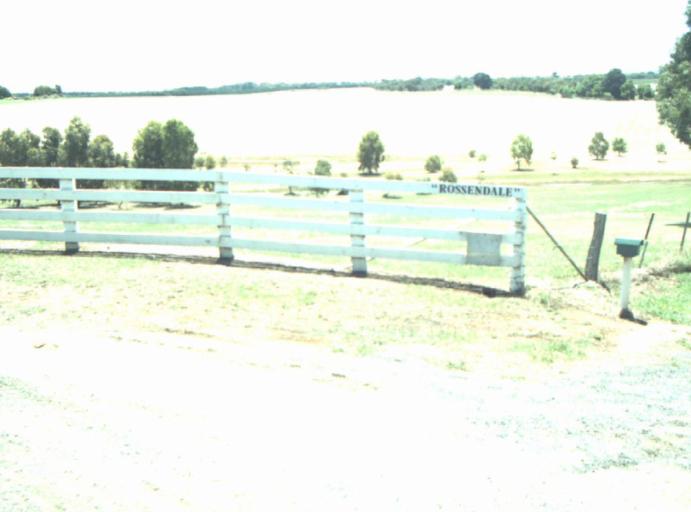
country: AU
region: Victoria
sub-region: Greater Geelong
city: Clifton Springs
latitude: -38.2332
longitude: 144.5799
